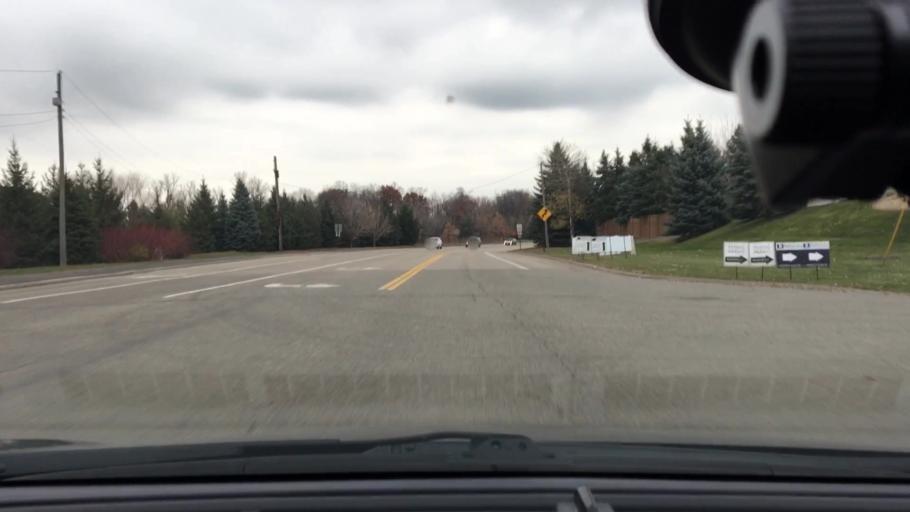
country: US
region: Minnesota
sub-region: Hennepin County
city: Corcoran
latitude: 45.0493
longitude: -93.5248
